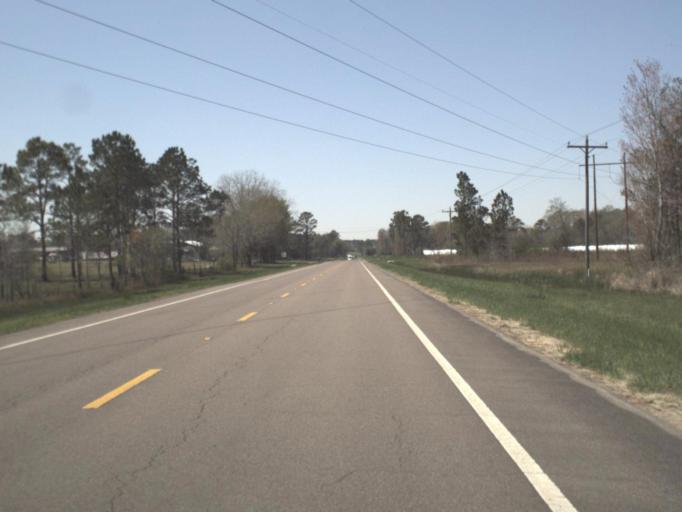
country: US
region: Alabama
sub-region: Geneva County
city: Hartford
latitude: 30.9583
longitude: -85.7101
